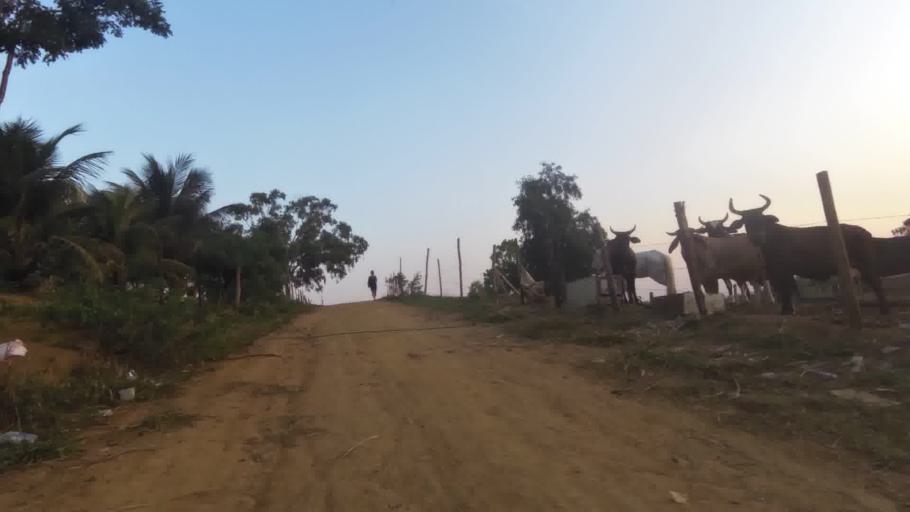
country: BR
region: Espirito Santo
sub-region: Piuma
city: Piuma
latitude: -20.8250
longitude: -40.7224
